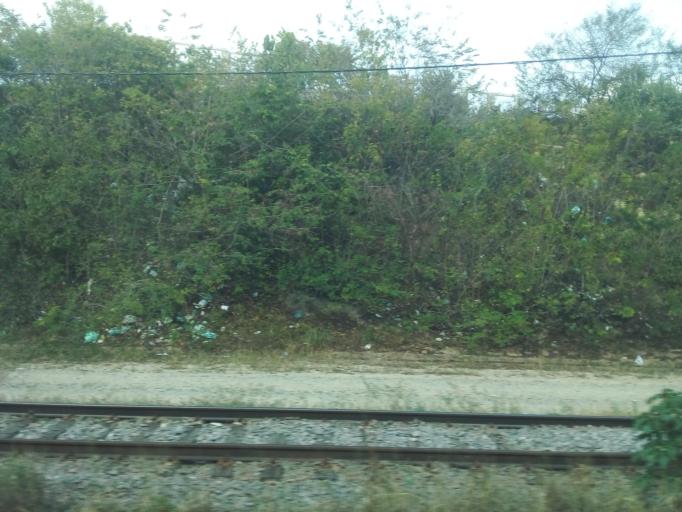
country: BR
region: Maranhao
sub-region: Sao Luis
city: Sao Luis
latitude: -2.6223
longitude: -44.3101
